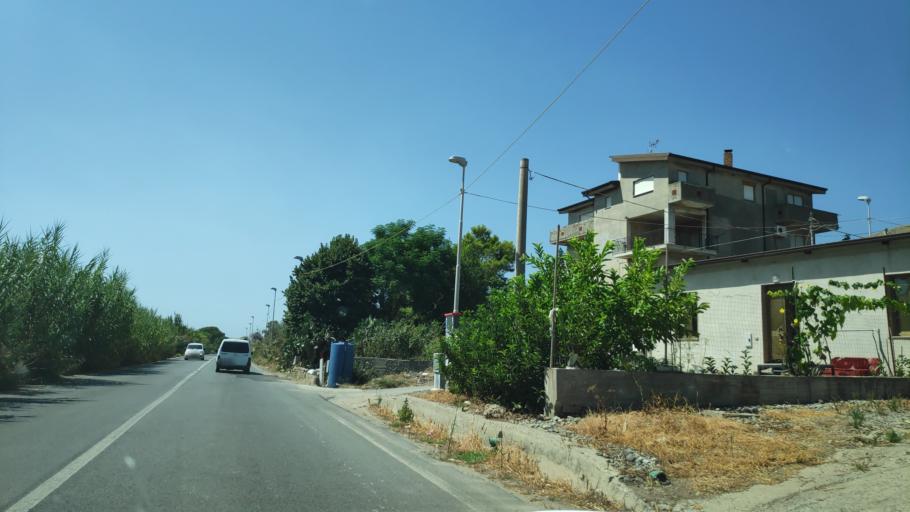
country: IT
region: Calabria
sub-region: Provincia di Reggio Calabria
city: Brancaleone-Marina
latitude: 37.9796
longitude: 16.1136
